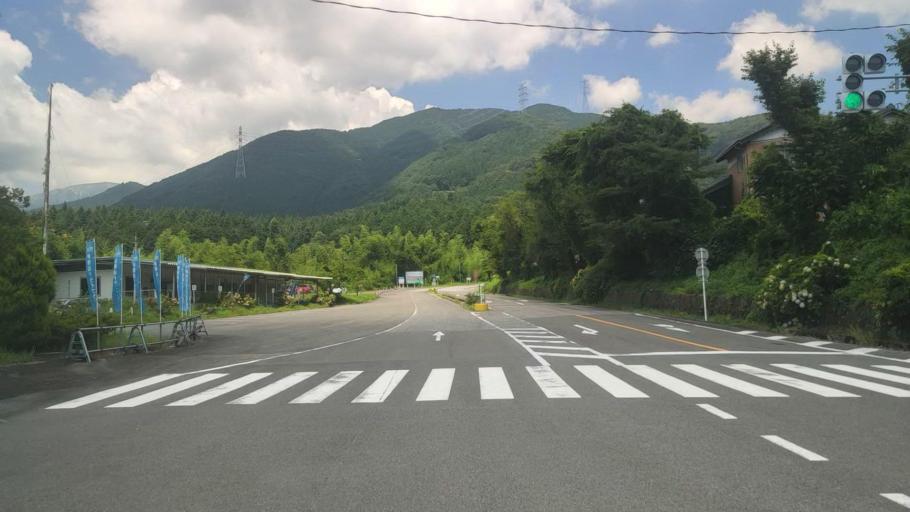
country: JP
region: Gifu
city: Tarui
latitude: 35.3714
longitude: 136.4492
